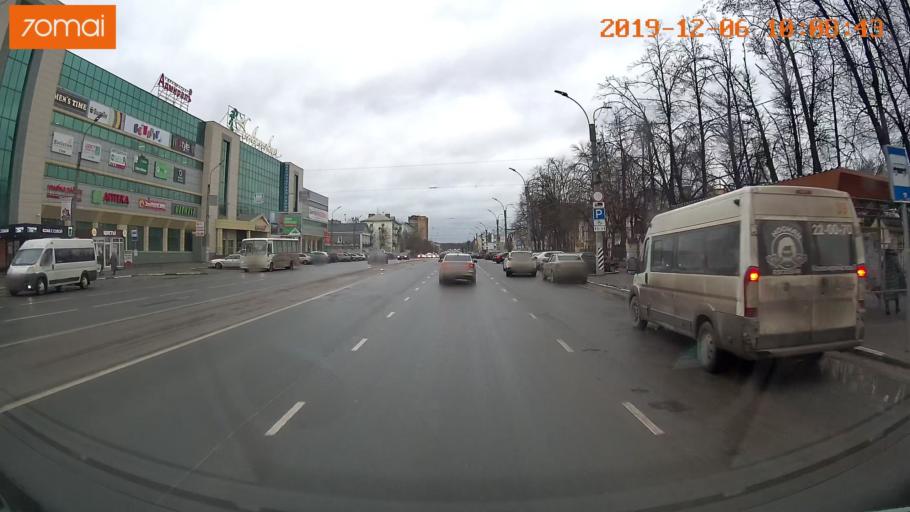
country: RU
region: Ivanovo
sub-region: Gorod Ivanovo
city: Ivanovo
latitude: 57.0173
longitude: 40.9694
